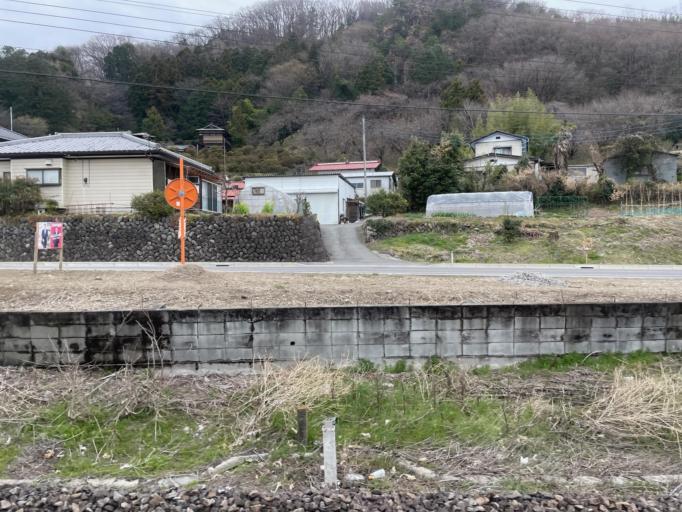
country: JP
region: Gunma
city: Shibukawa
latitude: 36.5187
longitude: 139.0293
